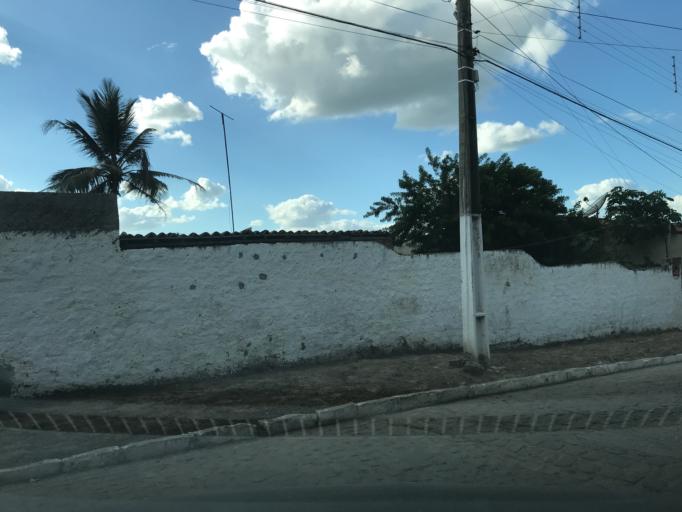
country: BR
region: Pernambuco
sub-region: Bezerros
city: Bezerros
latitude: -8.2416
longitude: -35.7576
